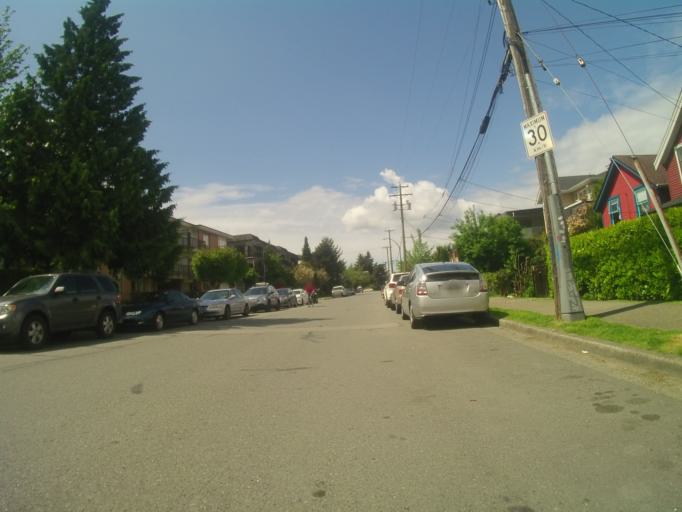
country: CA
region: British Columbia
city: Vancouver
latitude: 49.2653
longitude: -123.0930
